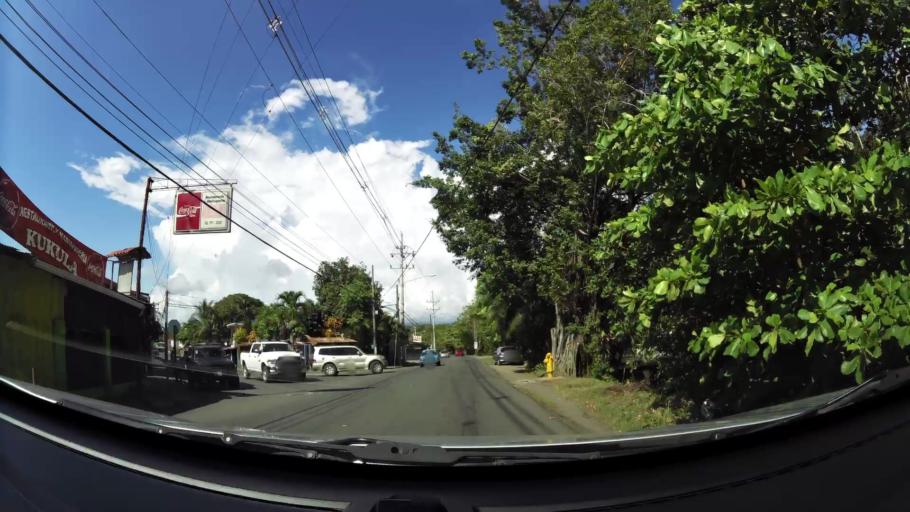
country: CR
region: Puntarenas
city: Quepos
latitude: 9.4358
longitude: -84.1644
